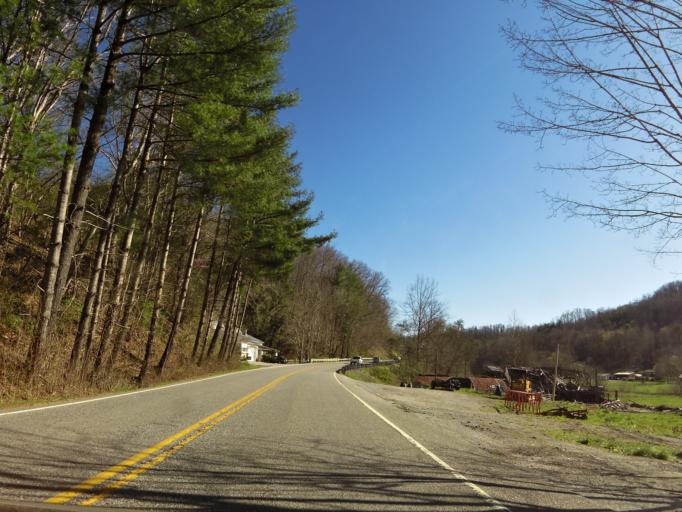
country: US
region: Tennessee
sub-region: Scott County
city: Oneida
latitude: 36.4663
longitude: -84.4778
